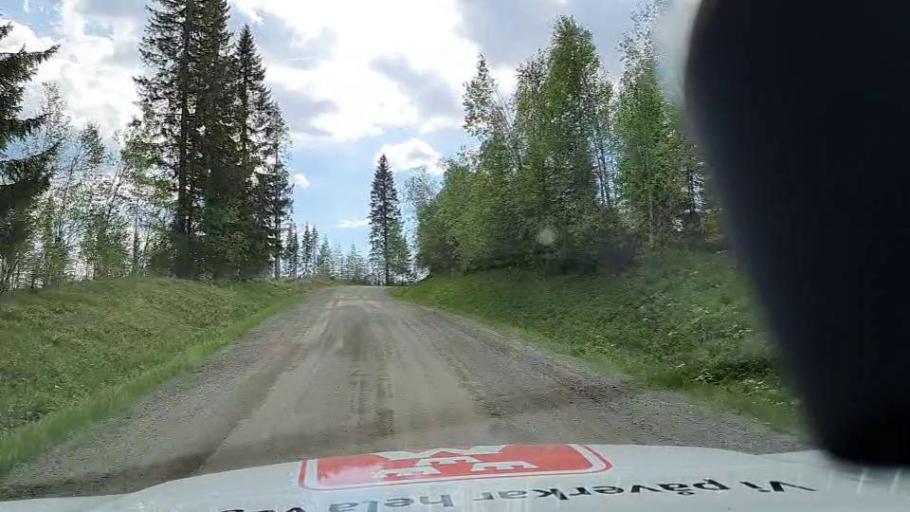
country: SE
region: Vaesterbotten
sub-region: Vilhelmina Kommun
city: Sjoberg
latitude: 64.5610
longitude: 15.8465
